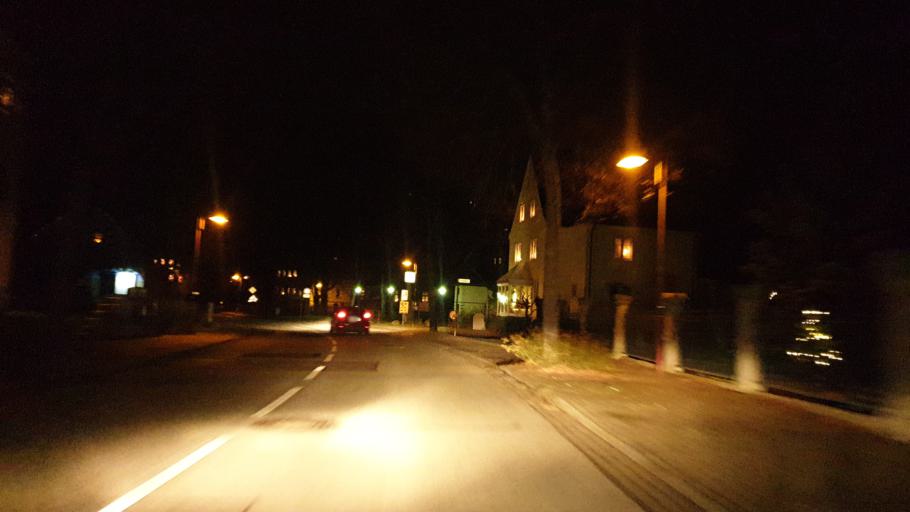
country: DE
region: Saxony
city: Lugau
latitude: 50.7214
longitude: 12.7472
